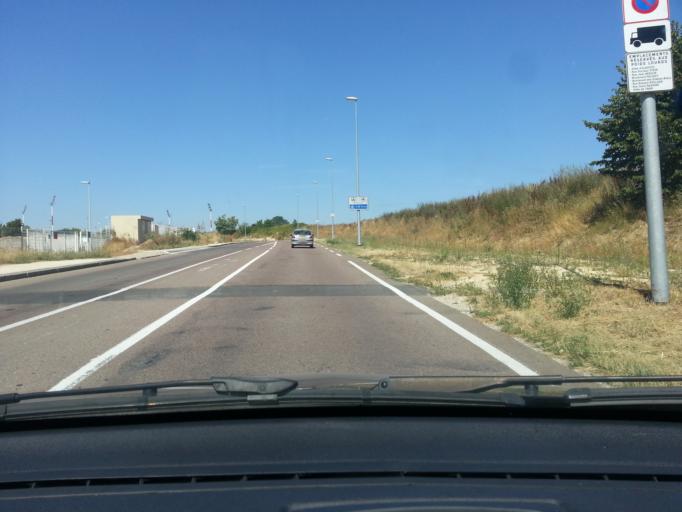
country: FR
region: Bourgogne
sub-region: Departement de la Cote-d'Or
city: Longvic
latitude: 47.3057
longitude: 5.0737
